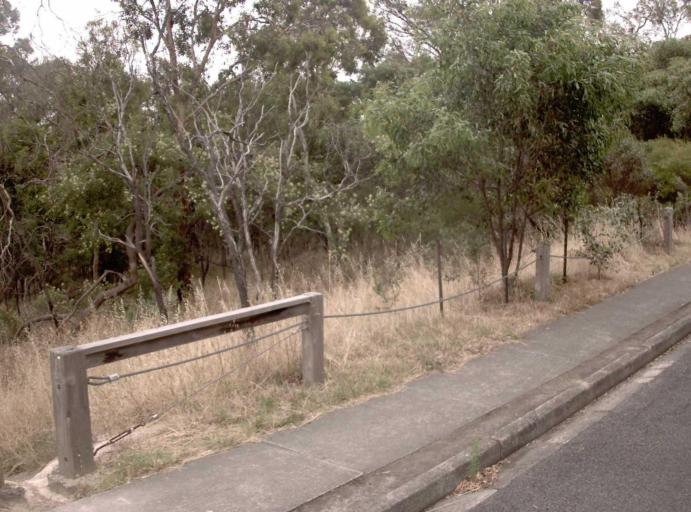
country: AU
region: Victoria
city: Abbotsford
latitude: -37.8017
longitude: 145.0111
